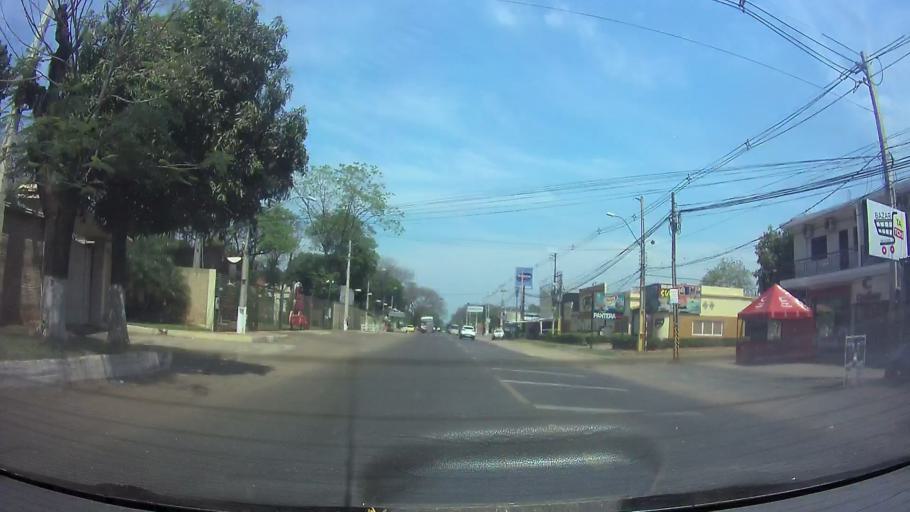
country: PY
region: Central
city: Capiata
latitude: -25.3757
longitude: -57.4768
